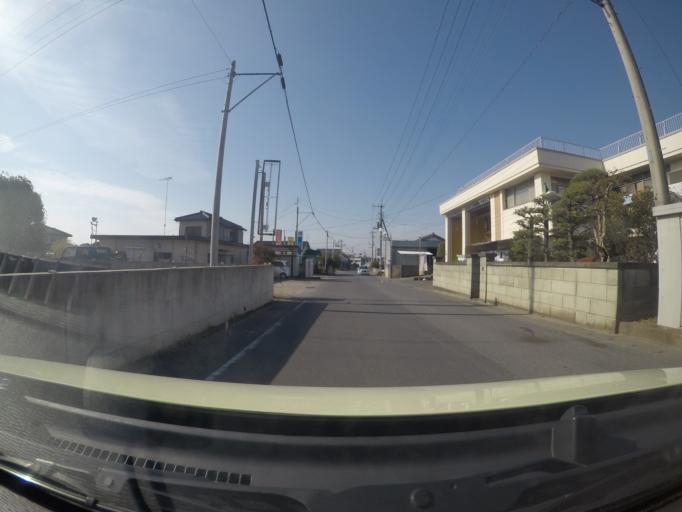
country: JP
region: Ibaraki
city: Tsukuba
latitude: 36.2076
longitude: 140.0770
